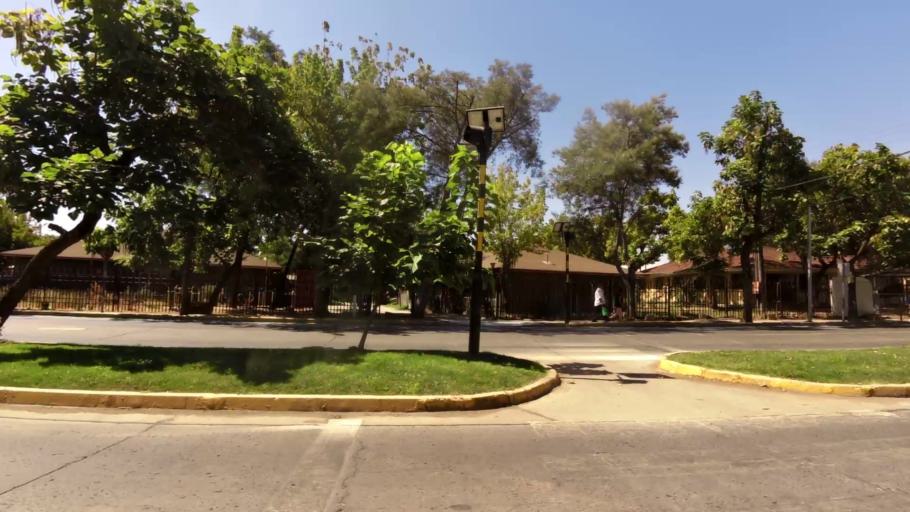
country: CL
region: Maule
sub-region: Provincia de Talca
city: Talca
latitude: -35.4124
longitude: -71.6553
